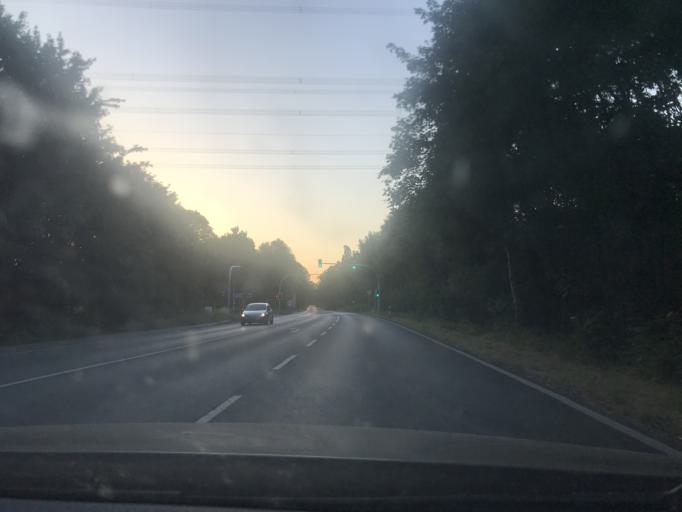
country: DE
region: North Rhine-Westphalia
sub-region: Regierungsbezirk Dusseldorf
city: Moers
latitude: 51.4949
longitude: 6.6317
